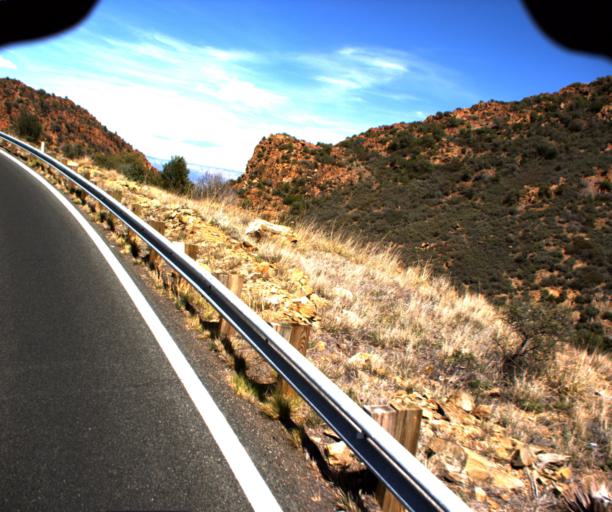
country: US
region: Arizona
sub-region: Yavapai County
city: Clarkdale
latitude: 34.7411
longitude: -112.1228
